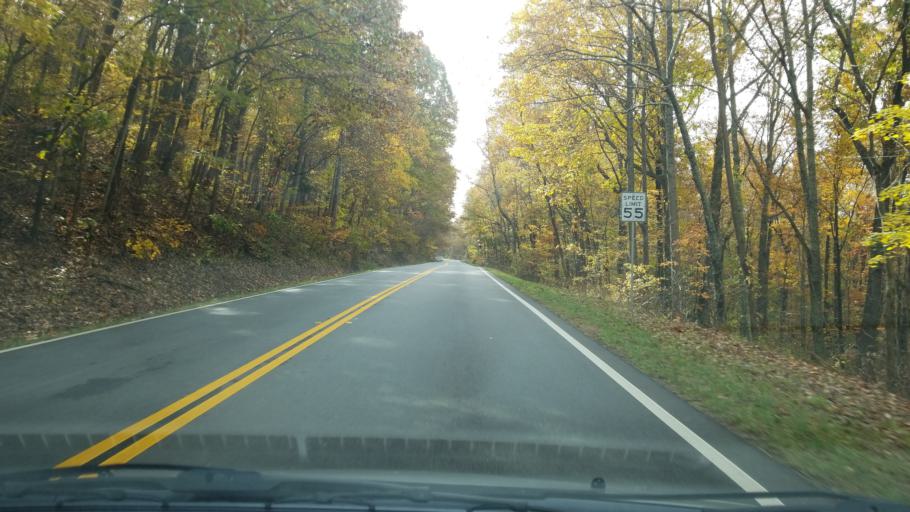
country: US
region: Georgia
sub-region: Dade County
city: Trenton
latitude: 34.8391
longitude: -85.4993
